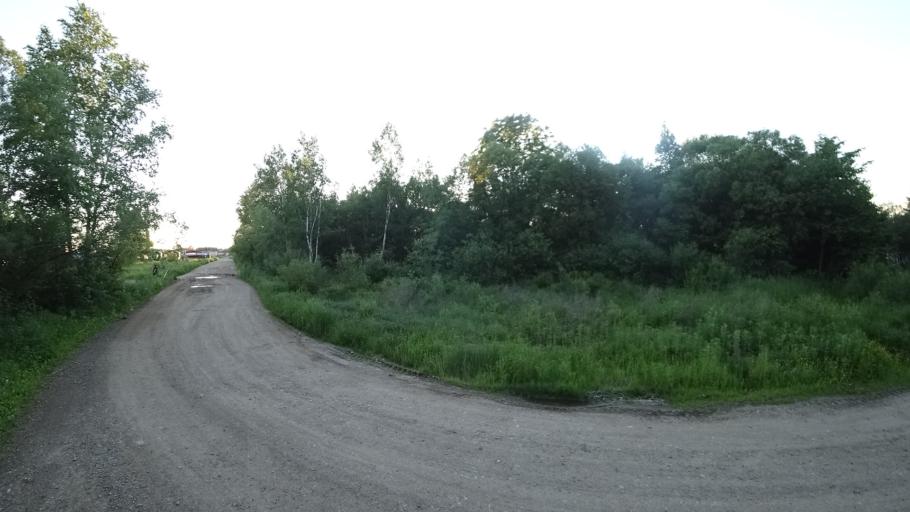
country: RU
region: Khabarovsk Krai
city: Khor
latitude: 47.8497
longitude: 134.9838
